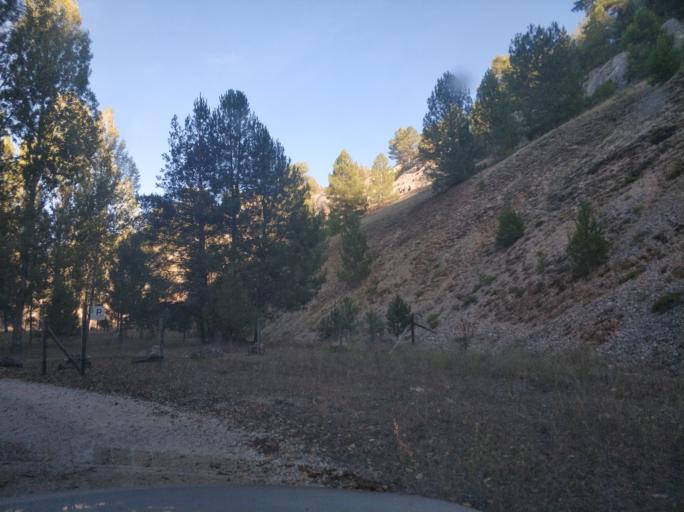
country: ES
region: Castille and Leon
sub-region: Provincia de Burgos
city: Hontoria del Pinar
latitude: 41.8410
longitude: -3.1599
